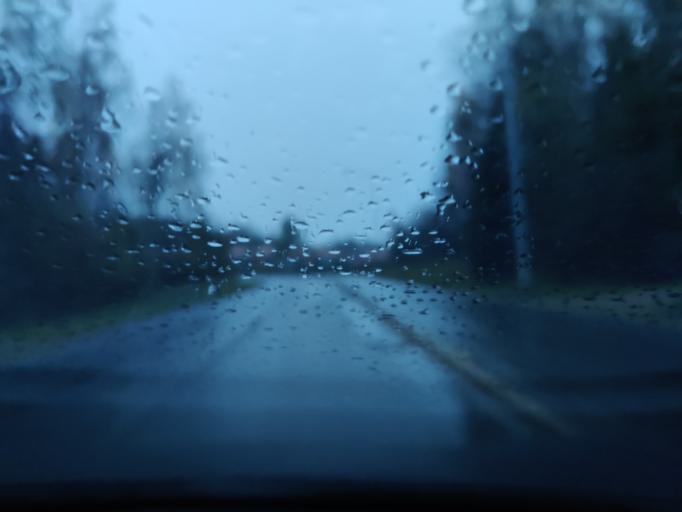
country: FI
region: Northern Savo
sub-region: Kuopio
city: Kuopio
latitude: 62.8307
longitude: 27.7157
